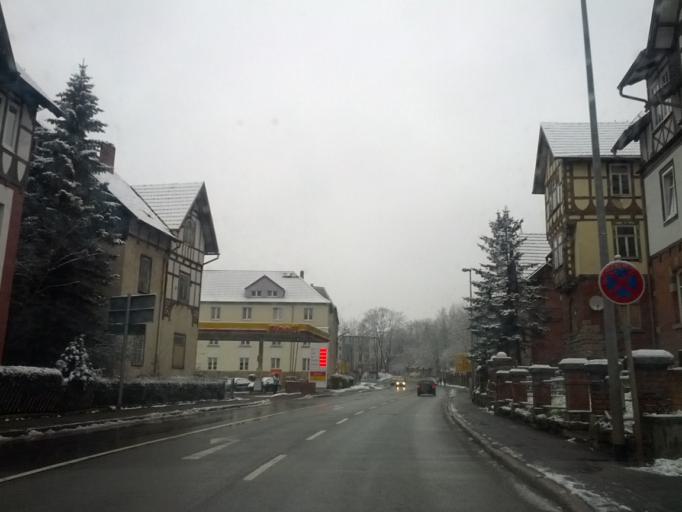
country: DE
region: Thuringia
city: Meiningen
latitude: 50.5823
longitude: 10.4172
